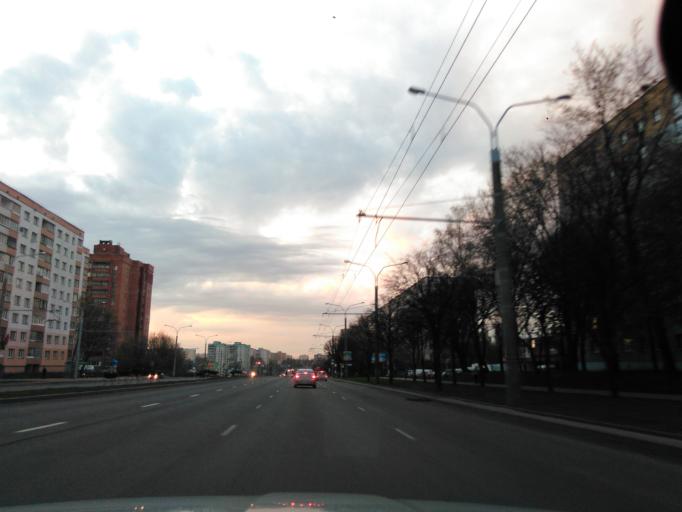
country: BY
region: Minsk
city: Novoye Medvezhino
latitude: 53.9044
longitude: 27.4965
